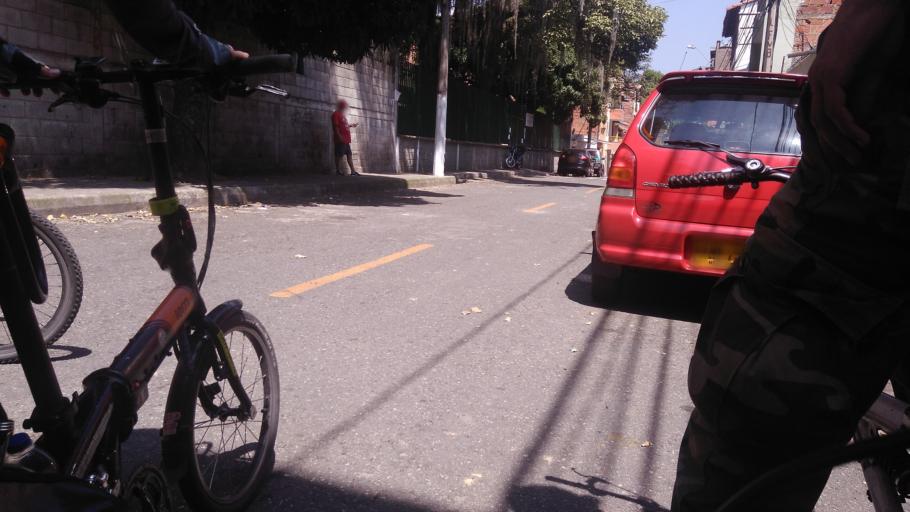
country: CO
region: Antioquia
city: Medellin
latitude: 6.2278
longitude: -75.5975
